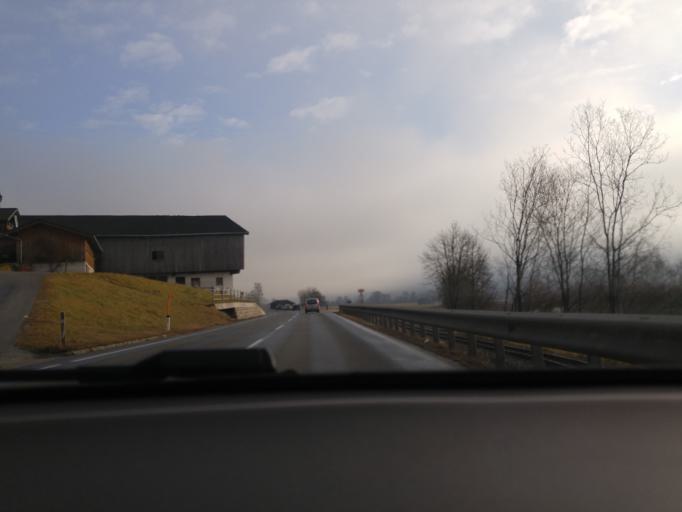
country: AT
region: Salzburg
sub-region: Politischer Bezirk Zell am See
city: Niedernsill
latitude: 47.2856
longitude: 12.6578
